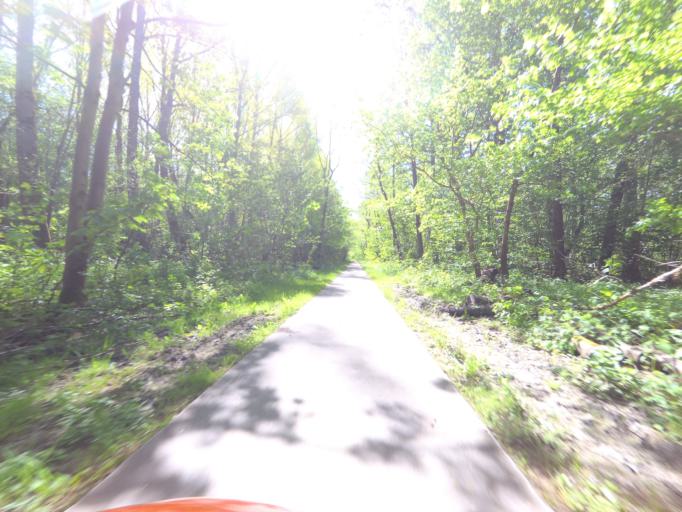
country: NL
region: Gelderland
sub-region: Gemeente Harderwijk
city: Harderwijk
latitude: 52.3929
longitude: 5.6295
